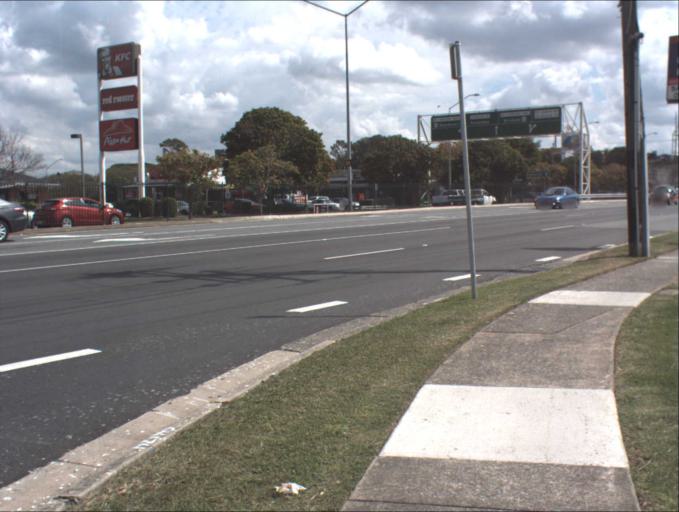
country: AU
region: Queensland
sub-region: Brisbane
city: Sunnybank Hills
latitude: -27.6605
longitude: 153.0400
